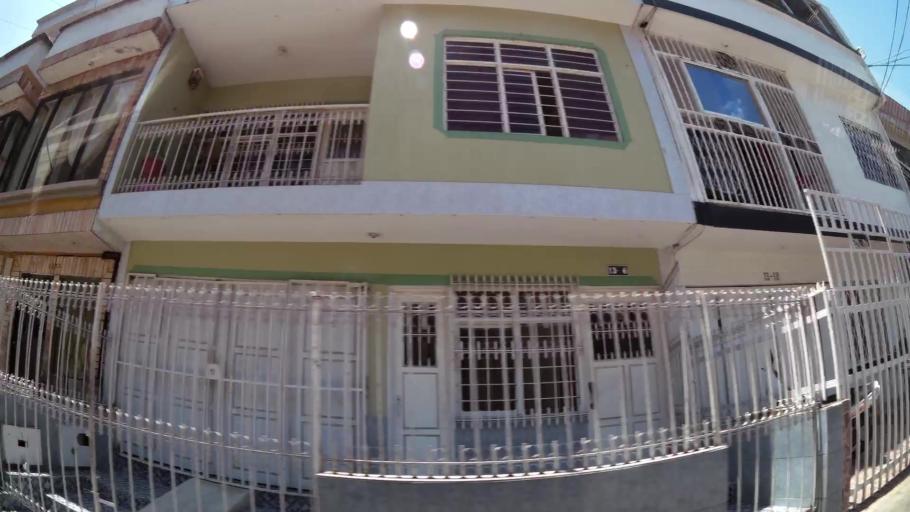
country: CO
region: Valle del Cauca
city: Cali
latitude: 3.4444
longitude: -76.4921
